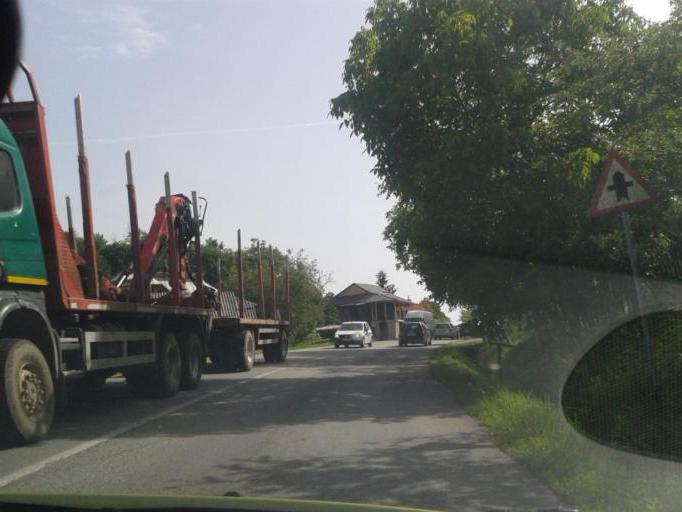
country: RO
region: Valcea
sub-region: Comuna Pietrari
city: Pietrari
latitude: 45.1009
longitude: 24.1326
